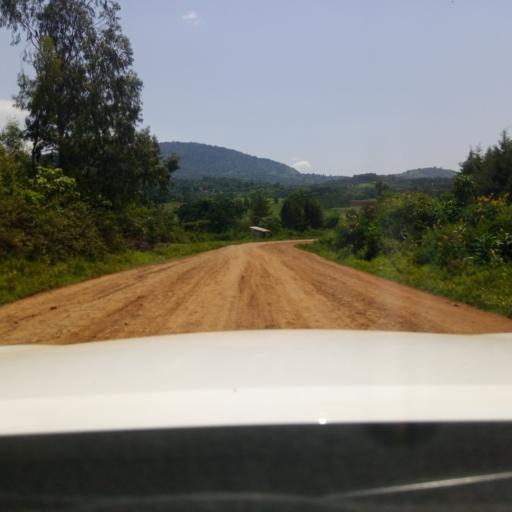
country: ET
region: Oromiya
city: Agaro
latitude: 8.1027
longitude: 36.9299
